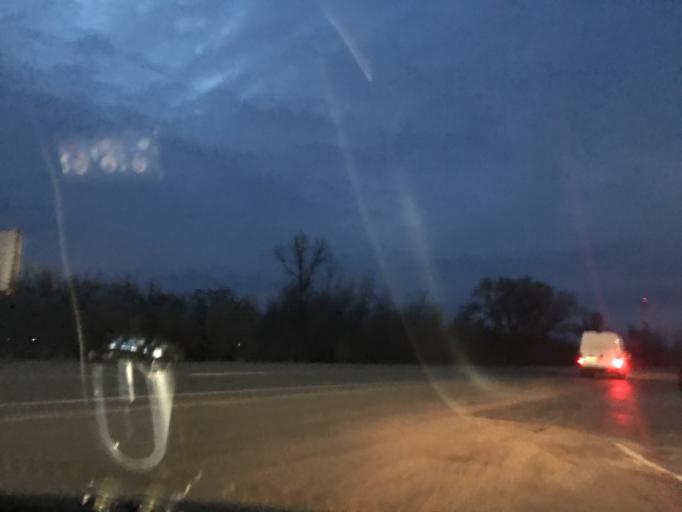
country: RU
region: Rostov
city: Bataysk
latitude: 47.0404
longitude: 39.7421
